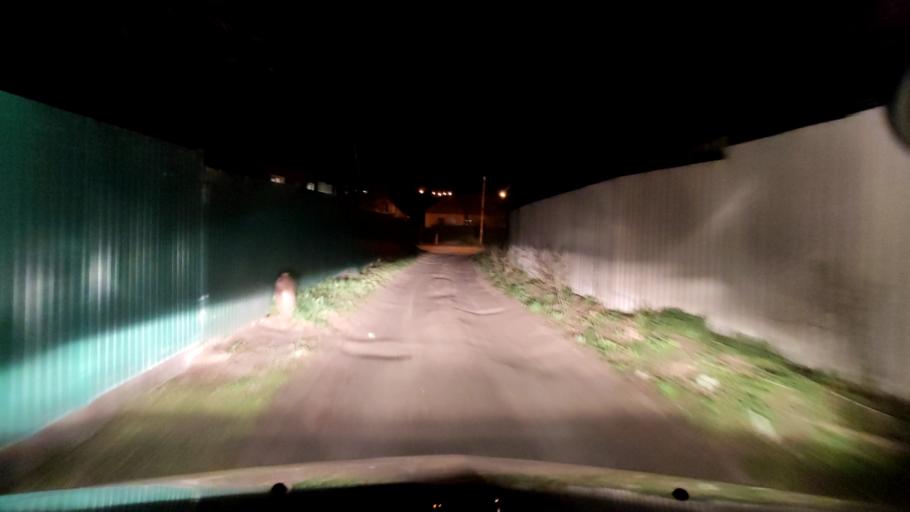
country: RU
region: Voronezj
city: Podgornoye
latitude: 51.7345
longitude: 39.1553
